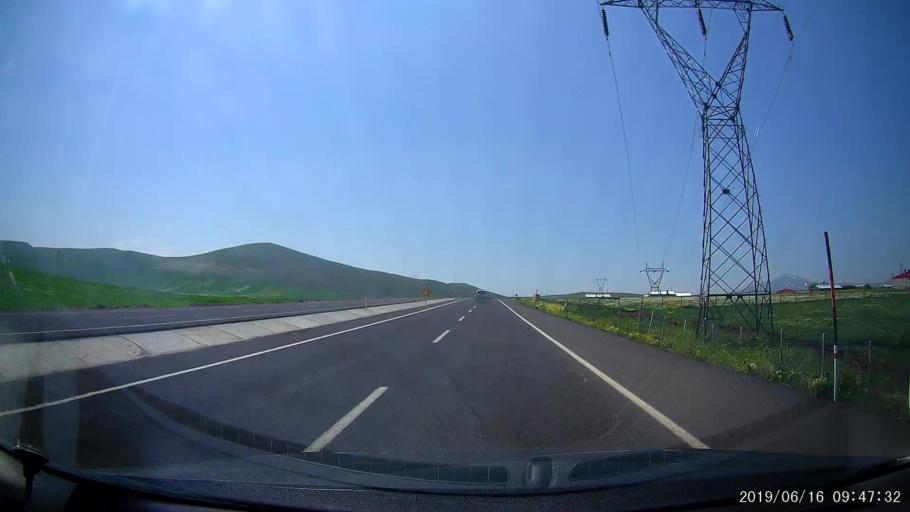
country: TR
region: Kars
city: Digor
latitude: 40.4460
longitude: 43.3447
